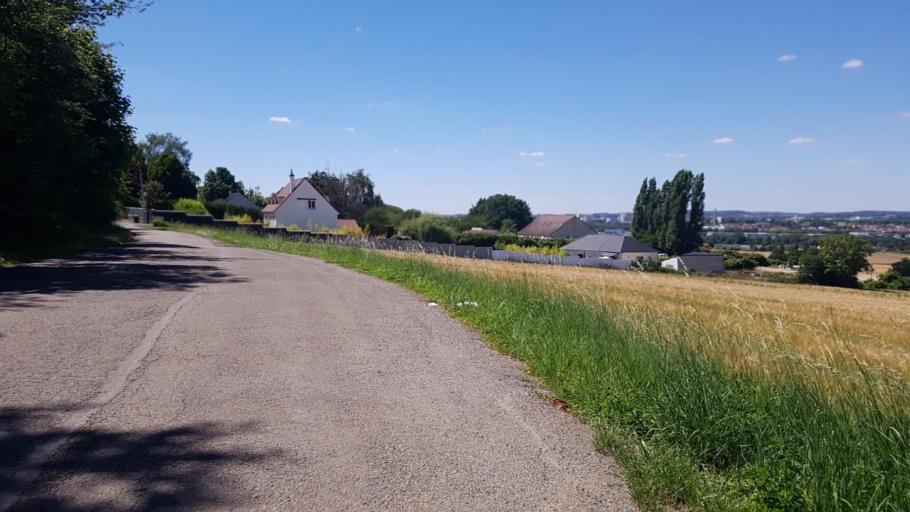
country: FR
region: Ile-de-France
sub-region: Departement de Seine-et-Marne
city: Fublaines
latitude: 48.9392
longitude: 2.9464
